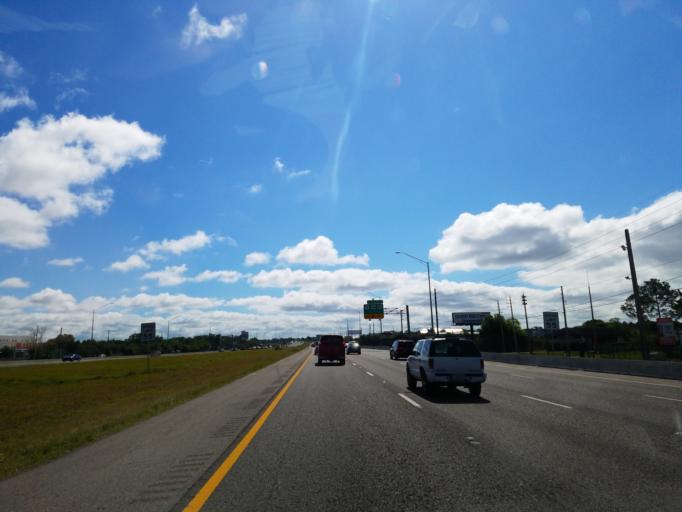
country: US
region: Florida
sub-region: Orange County
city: Holden Heights
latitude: 28.5092
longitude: -81.4099
